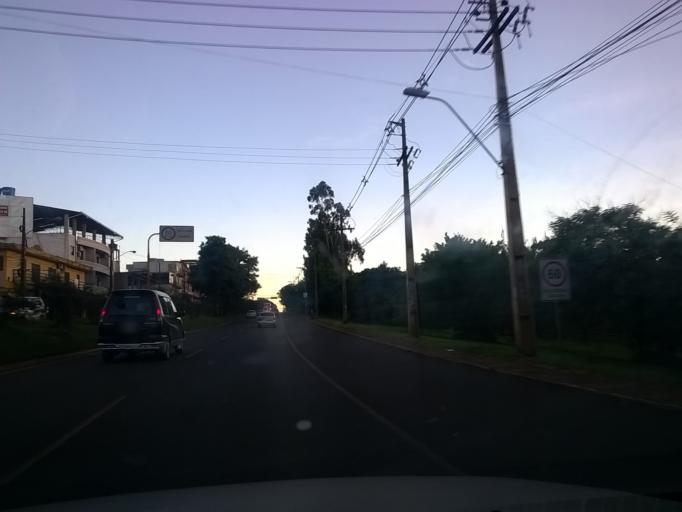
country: PY
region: Alto Parana
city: Ciudad del Este
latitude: -25.5144
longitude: -54.6416
